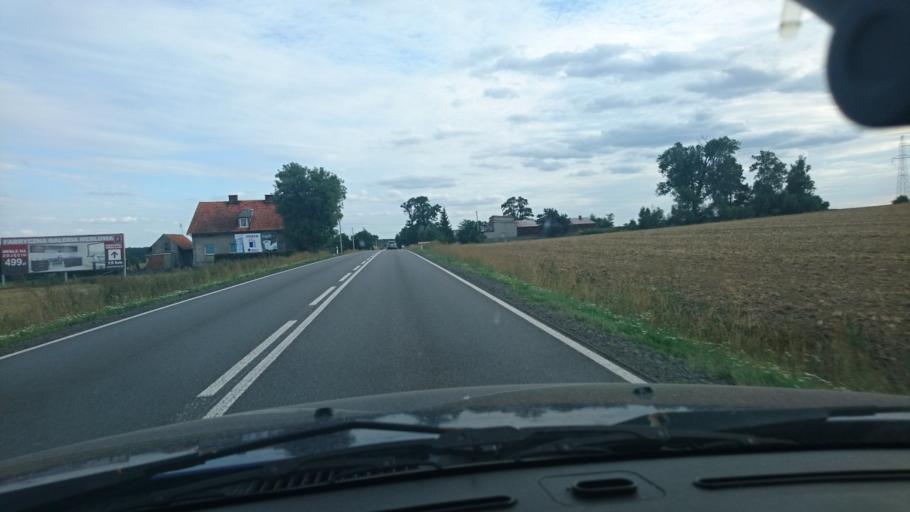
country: PL
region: Greater Poland Voivodeship
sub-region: Powiat ostrzeszowski
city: Ostrzeszow
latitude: 51.3610
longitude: 17.9463
